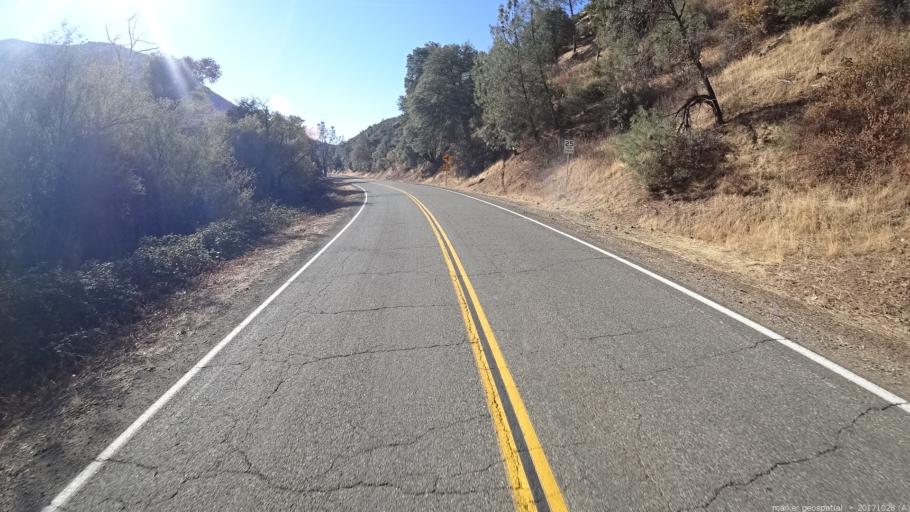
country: US
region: California
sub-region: Trinity County
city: Lewiston
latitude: 40.7103
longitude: -122.6379
